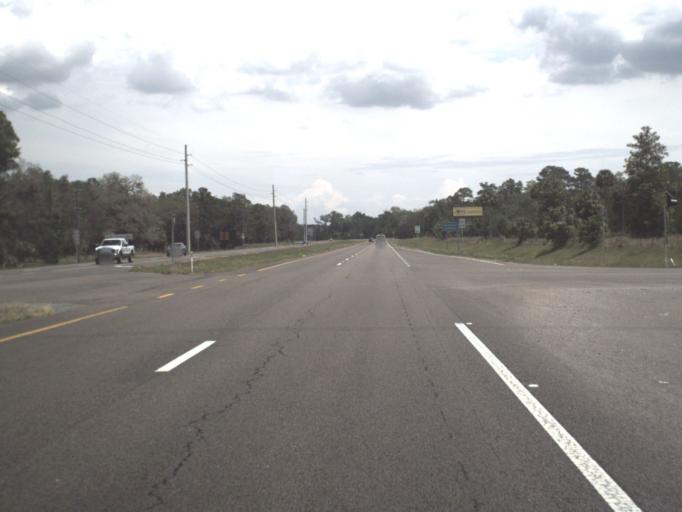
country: US
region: Florida
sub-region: Sumter County
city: Lake Panasoffkee
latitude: 28.8585
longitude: -82.1742
